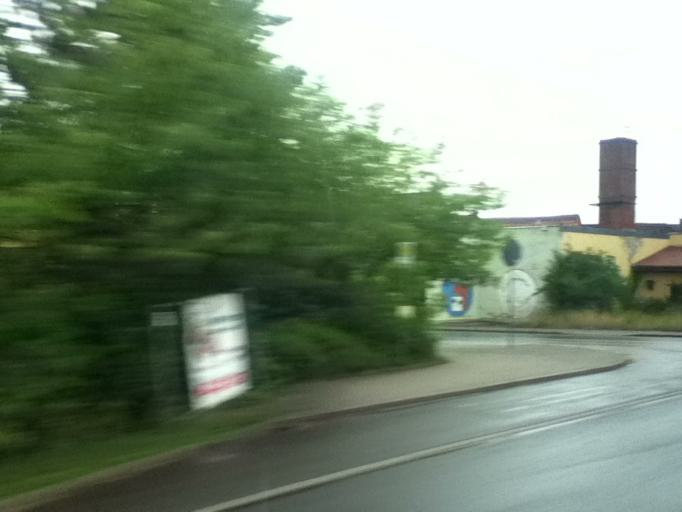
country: DE
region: Thuringia
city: Umpferstedt
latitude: 50.9760
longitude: 11.4090
